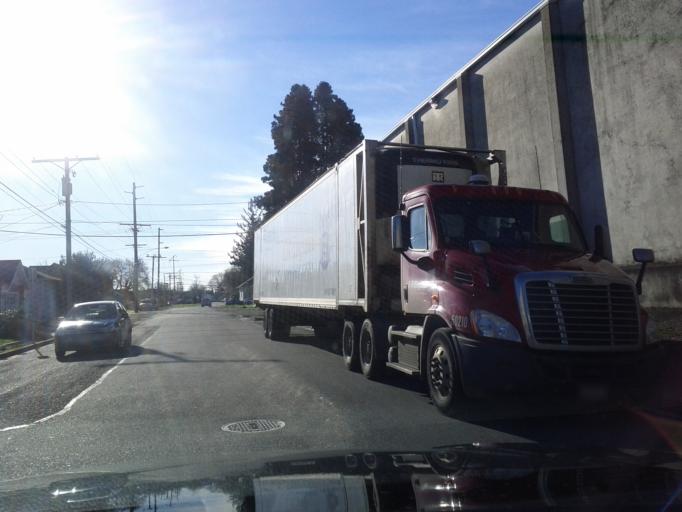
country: US
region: Washington
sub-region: Skagit County
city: Burlington
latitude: 48.4733
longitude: -122.3323
